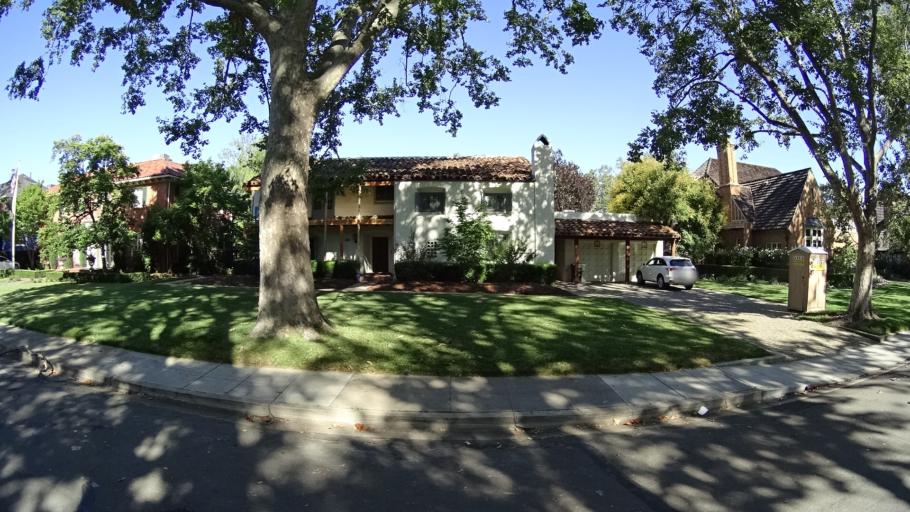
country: US
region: California
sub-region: Sacramento County
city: Sacramento
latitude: 38.5669
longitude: -121.4479
